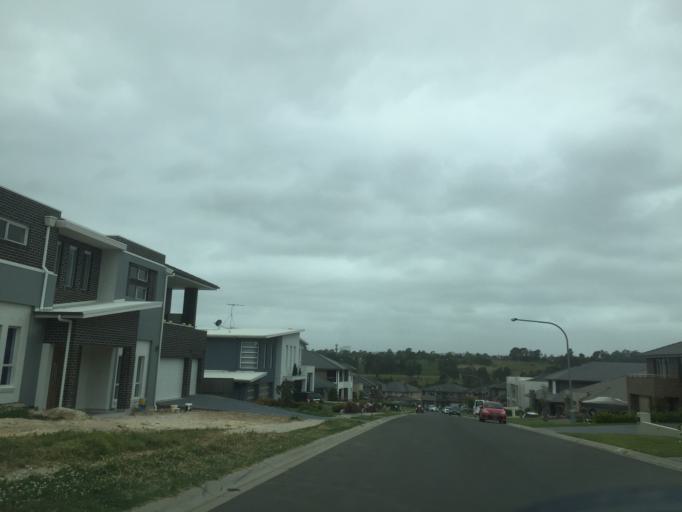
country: AU
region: New South Wales
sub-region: The Hills Shire
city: Beaumont Hills
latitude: -33.7211
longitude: 150.9522
